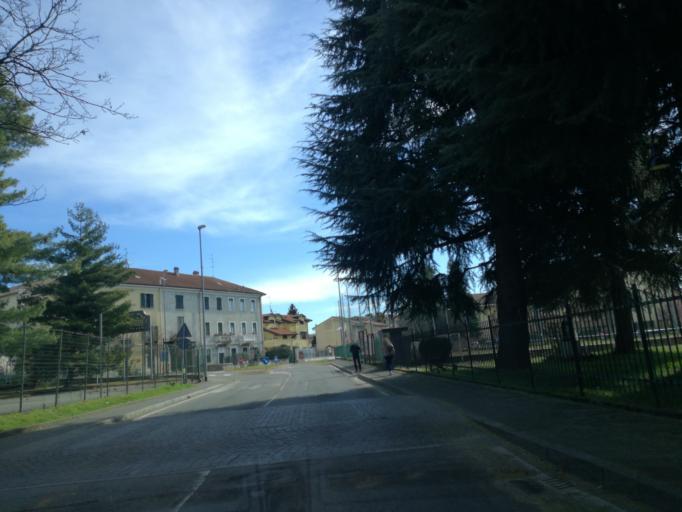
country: IT
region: Lombardy
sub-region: Provincia di Monza e Brianza
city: Lesmo
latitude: 45.6340
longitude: 9.3043
